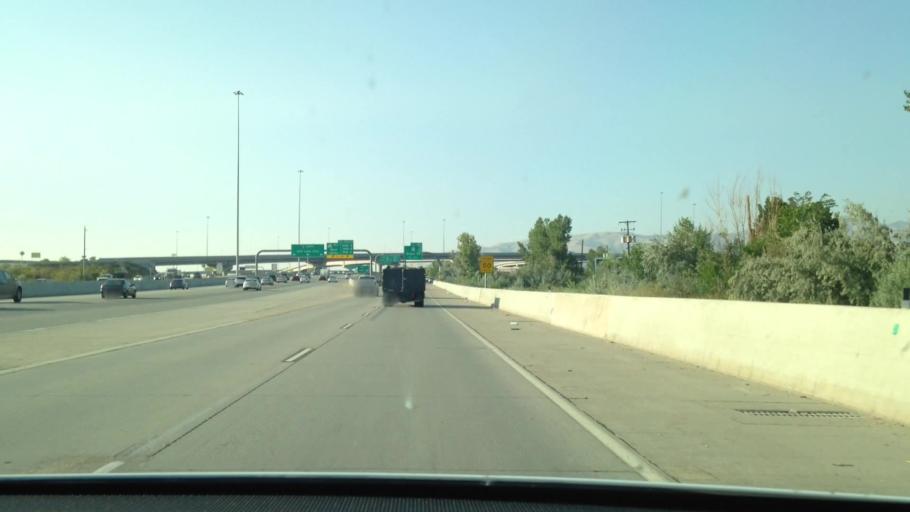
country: US
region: Utah
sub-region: Salt Lake County
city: South Salt Lake
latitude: 40.7136
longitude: -111.9033
